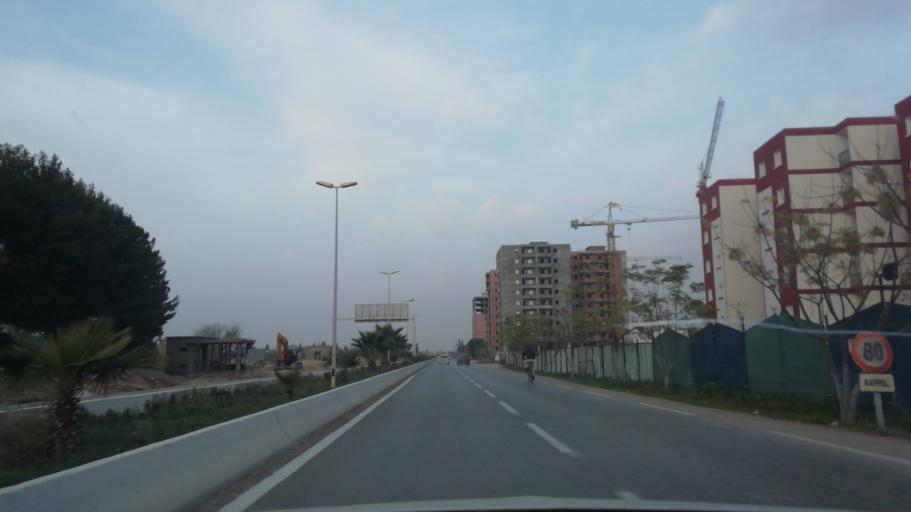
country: DZ
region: Sidi Bel Abbes
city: Sidi Bel Abbes
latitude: 35.2117
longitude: -0.6555
